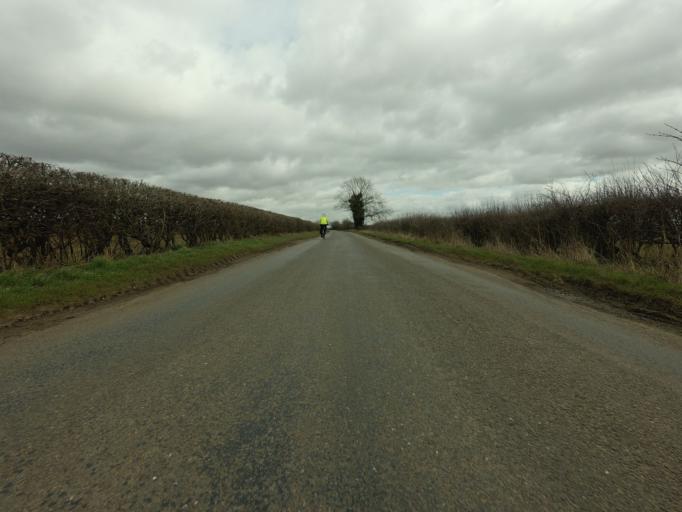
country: GB
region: England
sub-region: Lincolnshire
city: Barrowby
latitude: 52.8734
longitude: -0.6762
